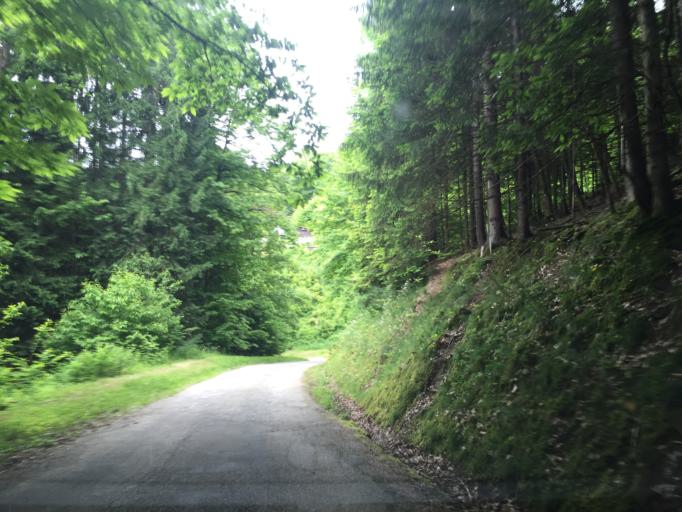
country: FR
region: Rhone-Alpes
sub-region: Departement de la Savoie
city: La Rochette
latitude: 45.4457
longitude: 6.1490
